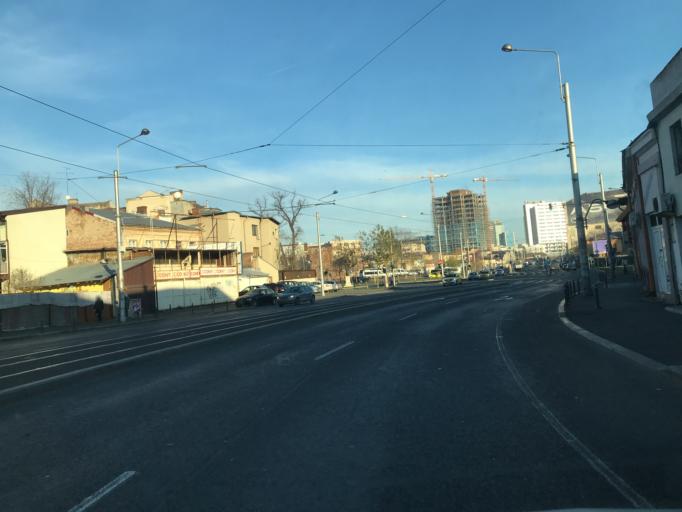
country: RO
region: Bucuresti
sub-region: Municipiul Bucuresti
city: Bucuresti
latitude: 44.4419
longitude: 26.0810
